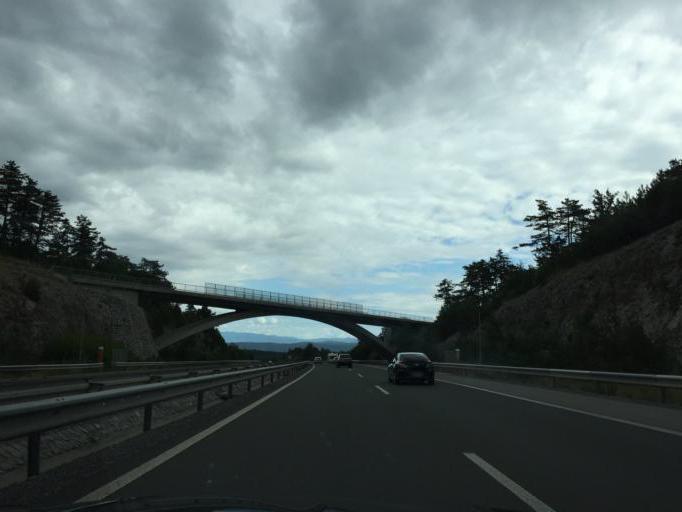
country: SI
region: Hrpelje-Kozina
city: Kozina
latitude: 45.6372
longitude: 13.9617
